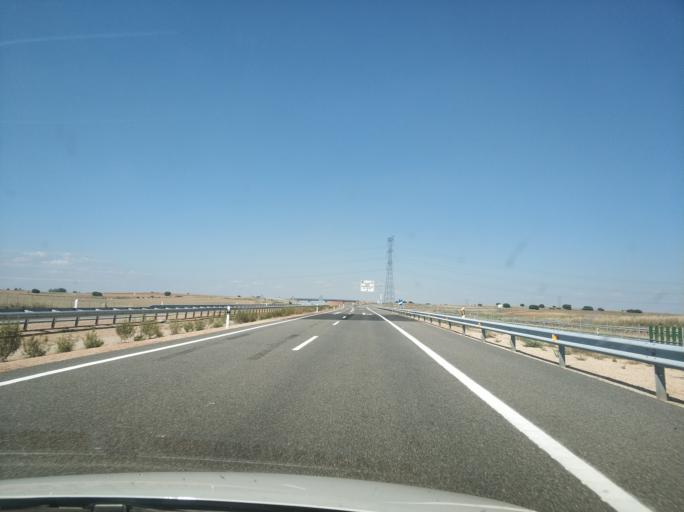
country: ES
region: Castille and Leon
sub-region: Provincia de Zamora
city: San Cebrian de Castro
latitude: 41.7181
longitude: -5.7832
